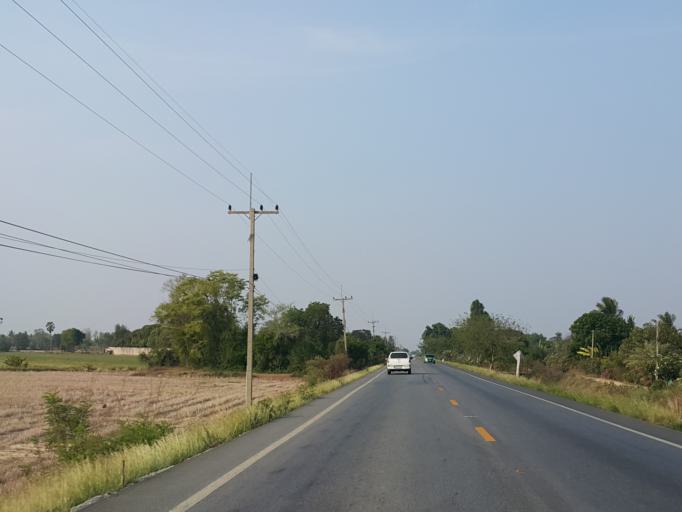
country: TH
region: Chai Nat
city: Hankha
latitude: 14.9734
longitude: 100.0997
